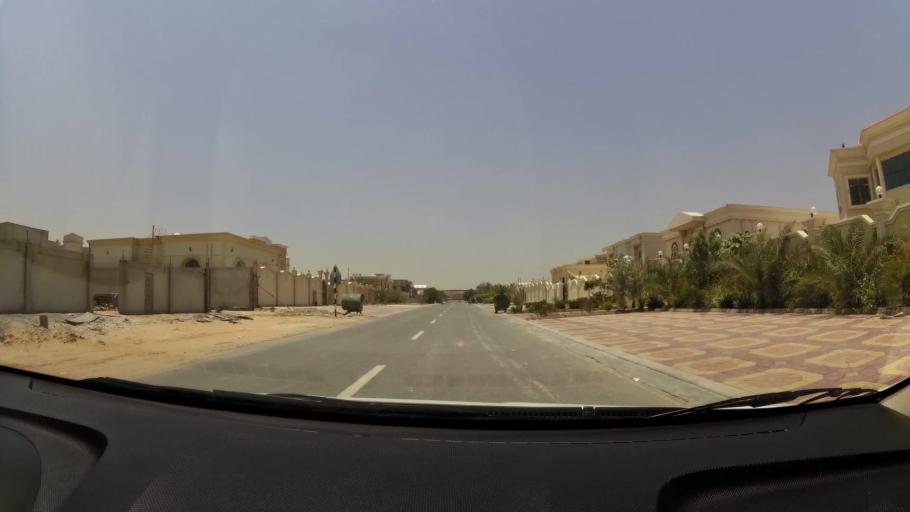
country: AE
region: Ajman
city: Ajman
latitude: 25.4059
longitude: 55.5036
